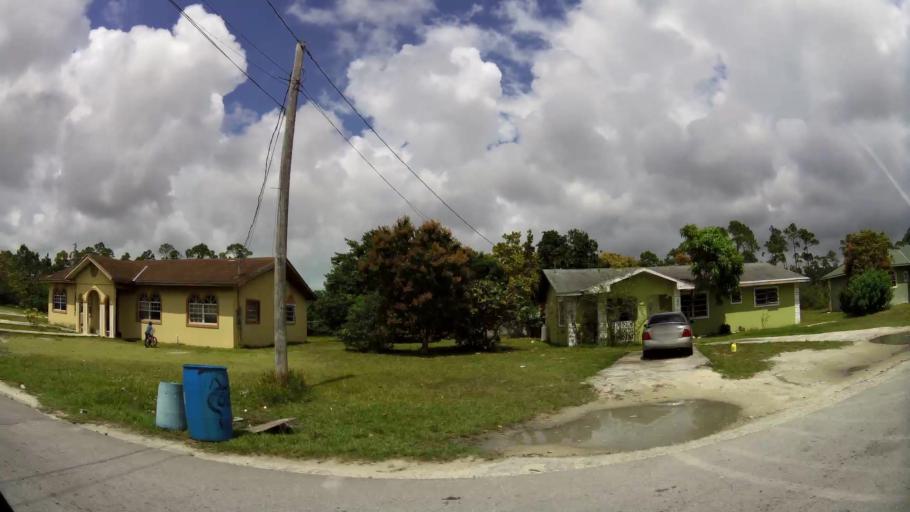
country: BS
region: Freeport
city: Lucaya
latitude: 26.5372
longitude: -78.6585
